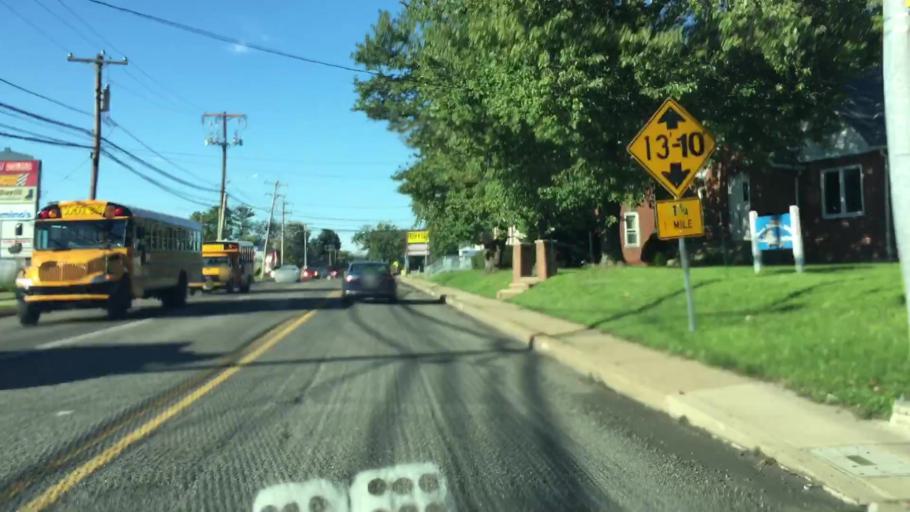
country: US
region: Pennsylvania
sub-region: Delaware County
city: Boothwyn
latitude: 39.8355
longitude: -75.4420
